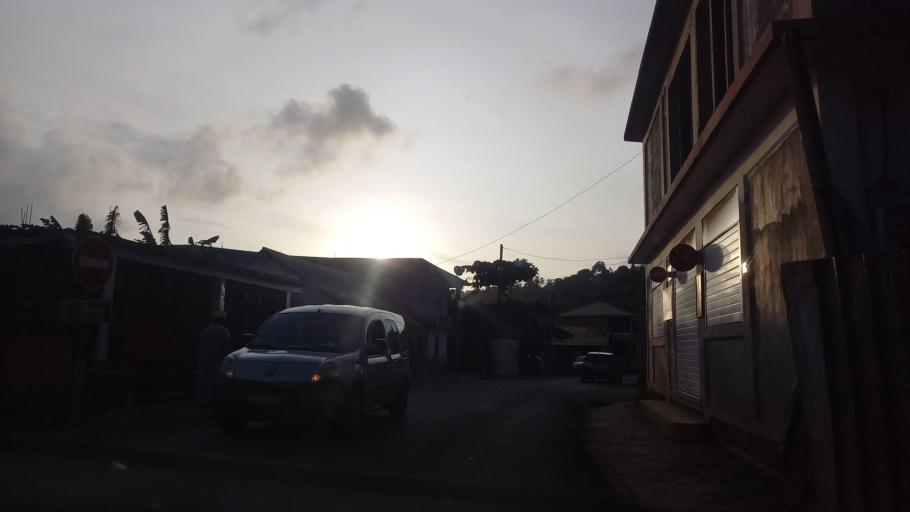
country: YT
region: M'Tsangamouji
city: M'Tsangamouji
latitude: -12.7611
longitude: 45.0870
